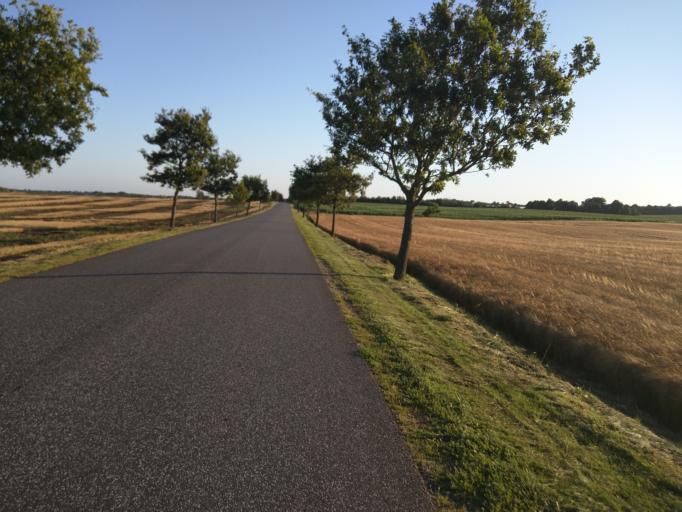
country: DK
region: Central Jutland
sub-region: Viborg Kommune
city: Bjerringbro
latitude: 56.4786
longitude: 9.5762
